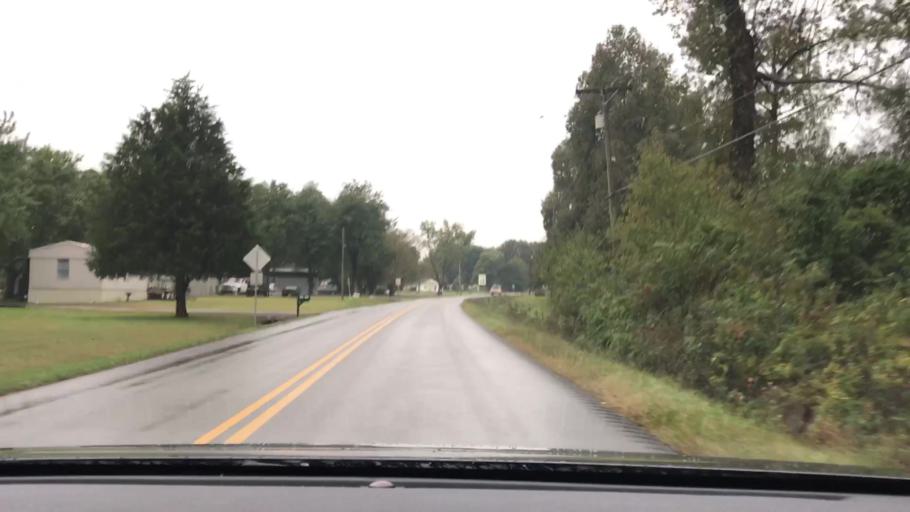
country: US
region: Kentucky
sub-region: Hopkins County
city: Madisonville
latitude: 37.3536
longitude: -87.3936
